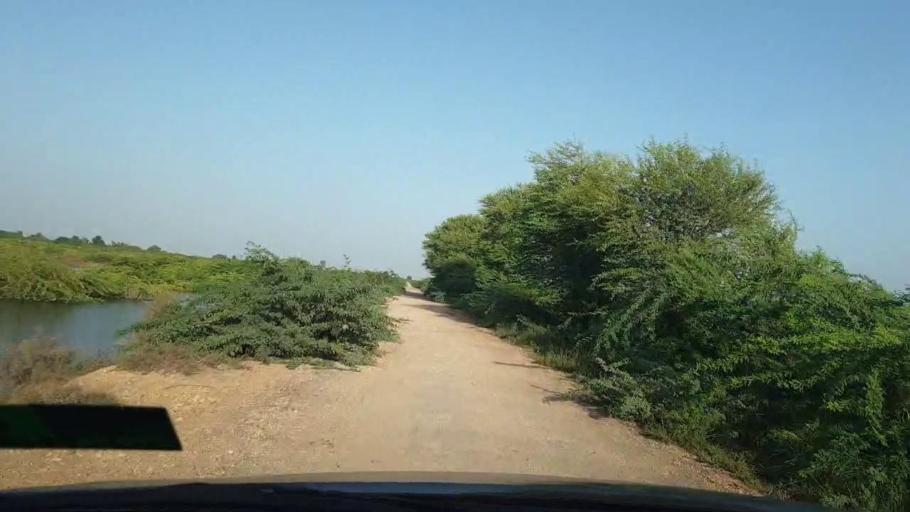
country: PK
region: Sindh
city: Naukot
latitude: 24.7262
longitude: 69.2308
